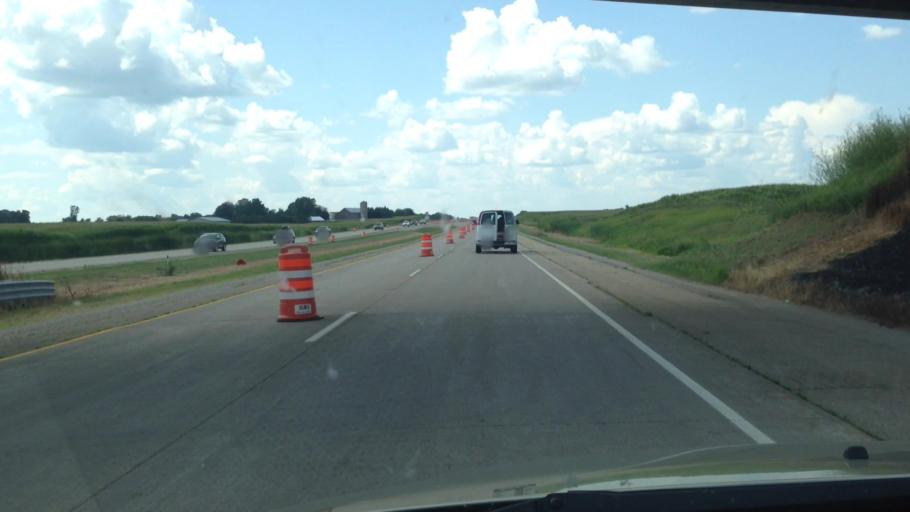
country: US
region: Wisconsin
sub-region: Brown County
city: Pulaski
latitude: 44.6892
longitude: -88.3238
